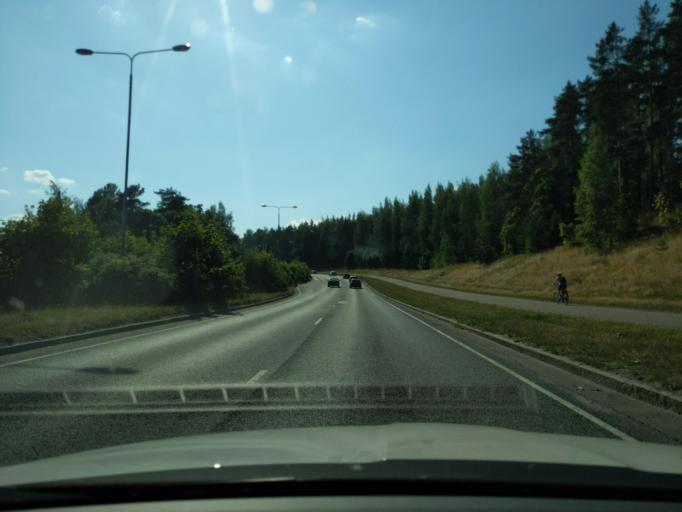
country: FI
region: Paijanne Tavastia
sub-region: Lahti
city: Lahti
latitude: 60.9813
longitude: 25.6257
